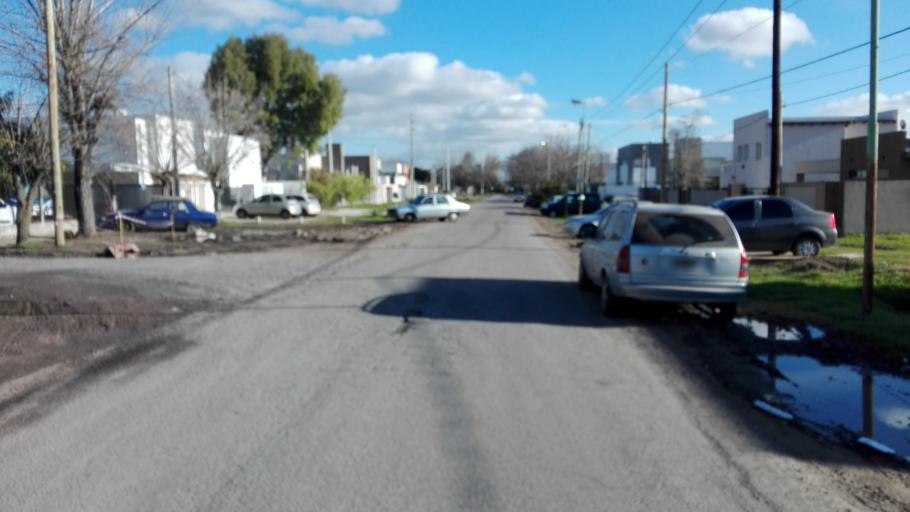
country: AR
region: Buenos Aires
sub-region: Partido de La Plata
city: La Plata
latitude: -34.9042
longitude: -58.0223
